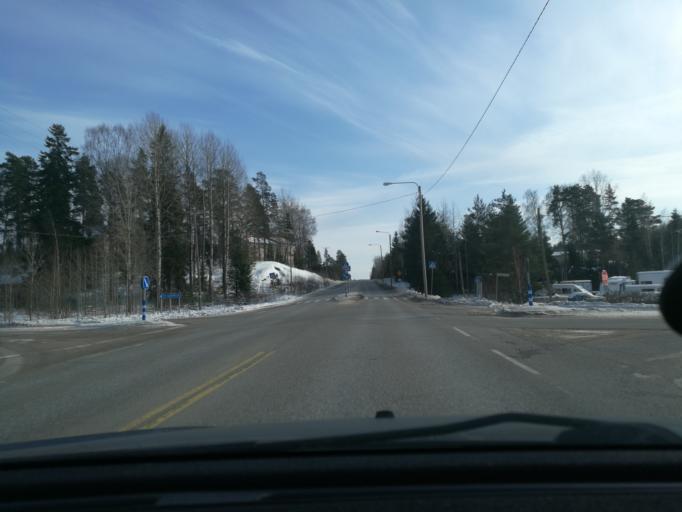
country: FI
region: Uusimaa
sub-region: Helsinki
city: Saukkola
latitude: 60.4007
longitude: 24.0653
